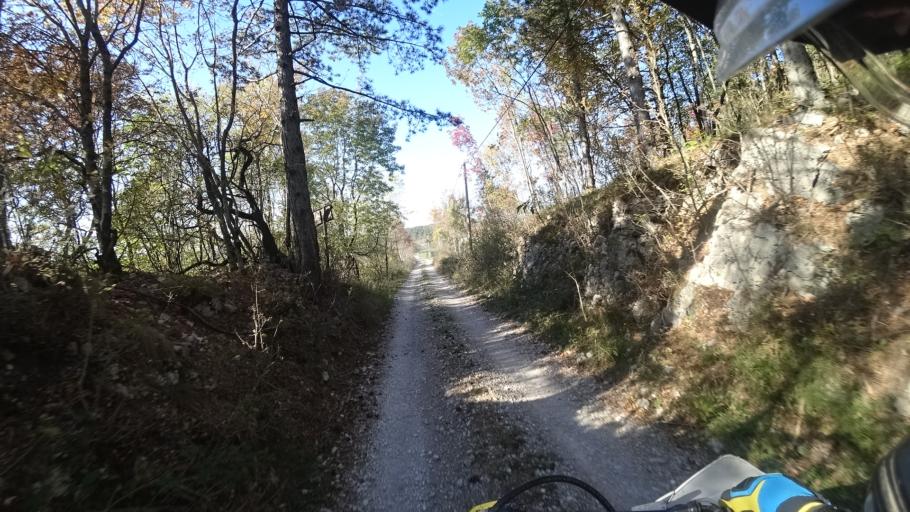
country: HR
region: Primorsko-Goranska
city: Klana
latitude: 45.4724
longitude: 14.3489
